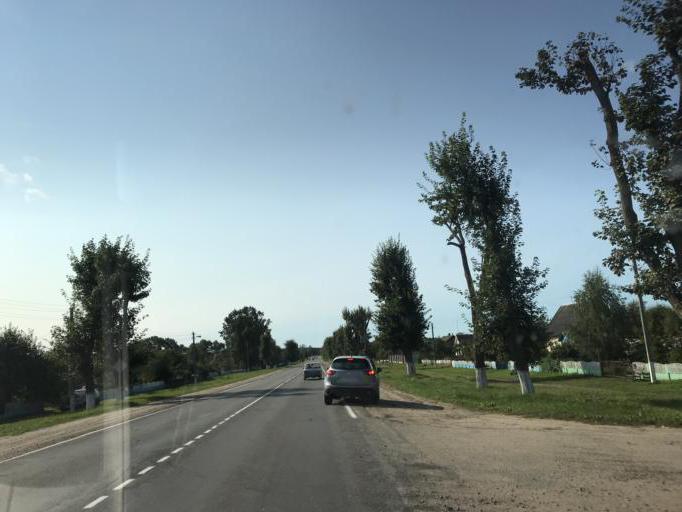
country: BY
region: Mogilev
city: Buynichy
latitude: 53.8332
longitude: 30.2450
